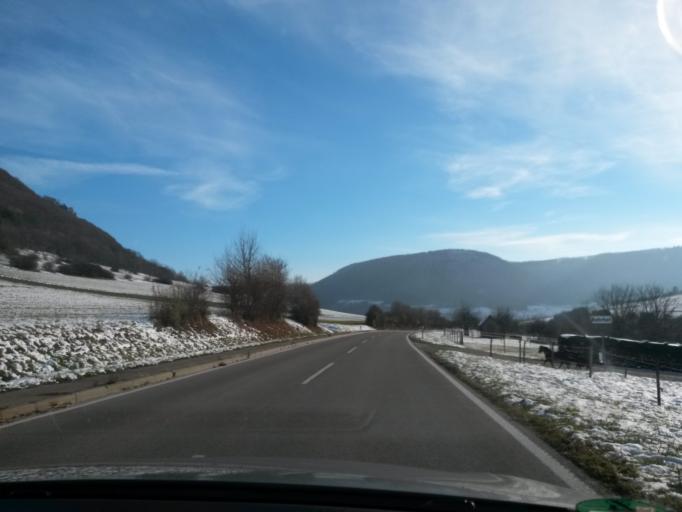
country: DE
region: Baden-Wuerttemberg
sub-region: Regierungsbezirk Stuttgart
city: Bad Uberkingen
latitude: 48.6187
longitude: 9.7586
